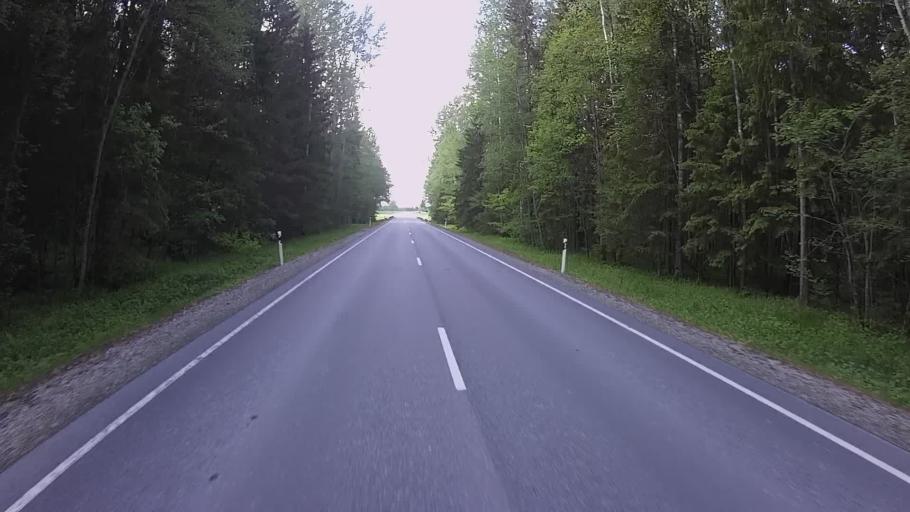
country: EE
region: Jogevamaa
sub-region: Mustvee linn
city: Mustvee
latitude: 58.8833
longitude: 26.8148
